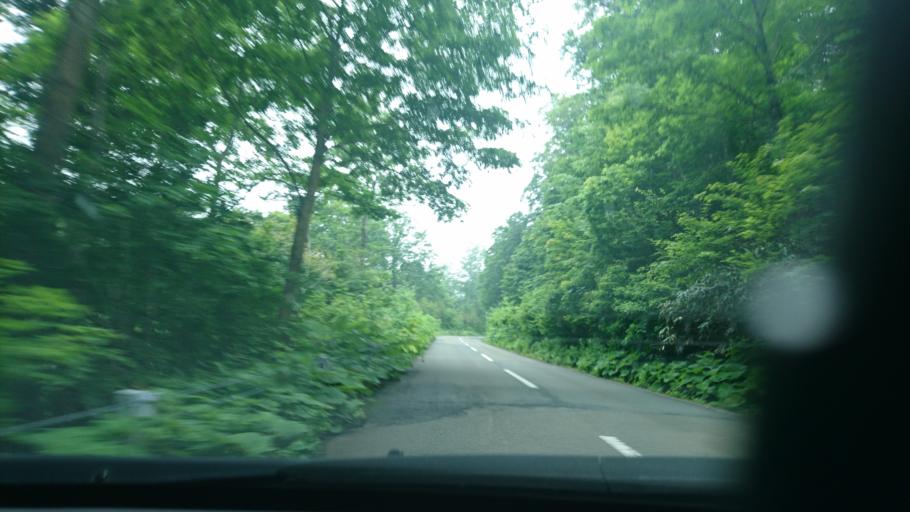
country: JP
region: Akita
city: Yuzawa
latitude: 39.1400
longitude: 140.7724
